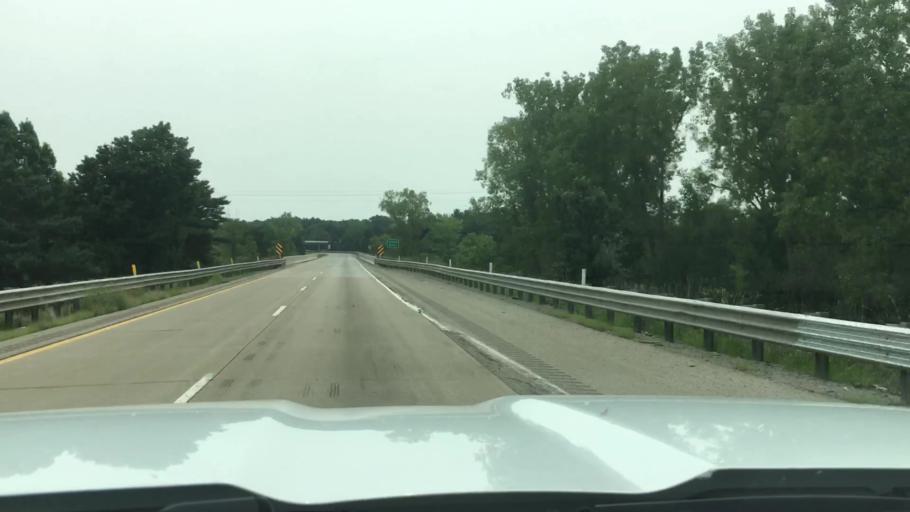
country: US
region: Michigan
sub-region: Eaton County
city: Dimondale
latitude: 42.6708
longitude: -84.6469
